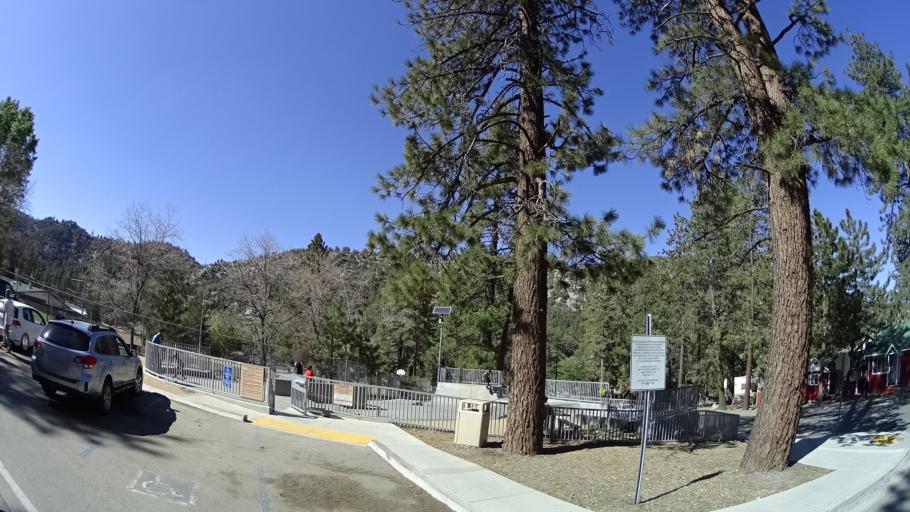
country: US
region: California
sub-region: San Bernardino County
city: Wrightwood
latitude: 34.3601
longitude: -117.6355
